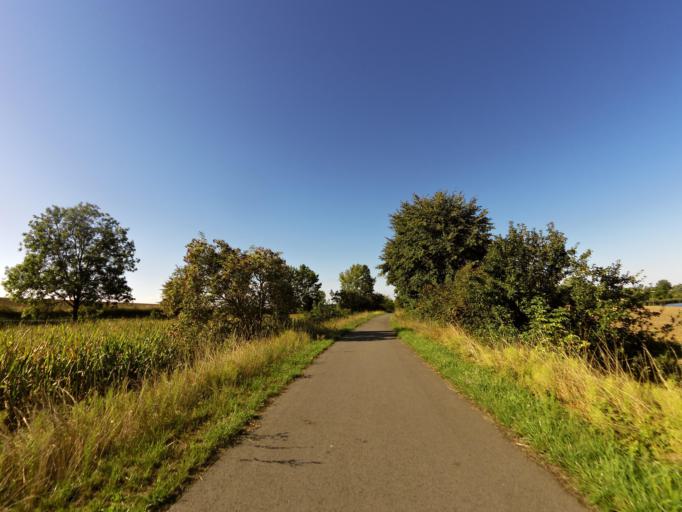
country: PL
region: West Pomeranian Voivodeship
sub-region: Powiat choszczenski
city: Choszczno
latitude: 53.1256
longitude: 15.3680
